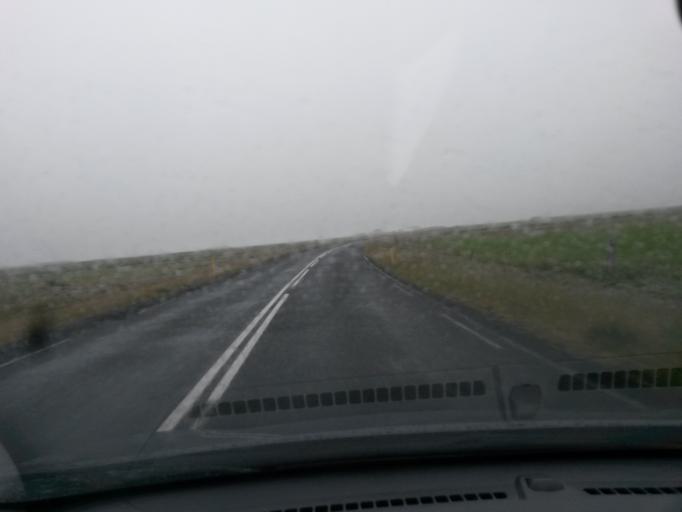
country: IS
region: South
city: Vestmannaeyjar
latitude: 63.4315
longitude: -19.1796
